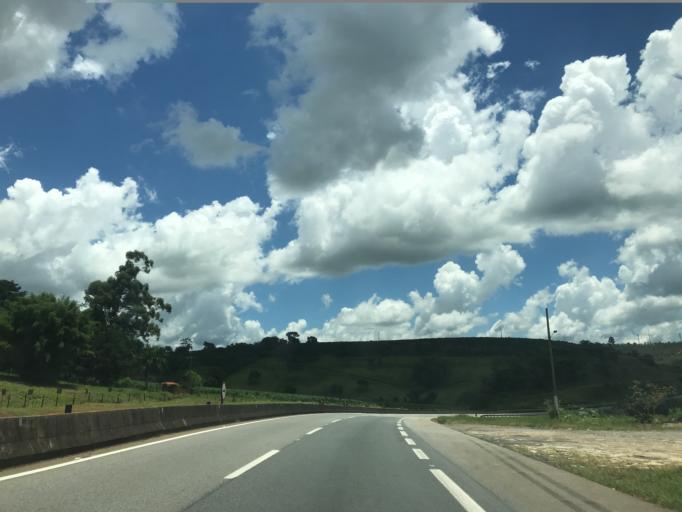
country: BR
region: Minas Gerais
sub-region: Nepomuceno
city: Nepomuceno
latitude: -21.4075
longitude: -45.2117
